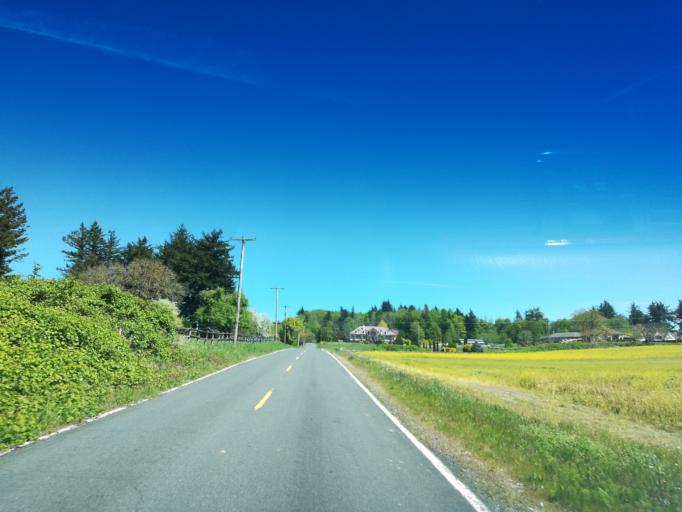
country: US
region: Oregon
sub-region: Multnomah County
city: Troutdale
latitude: 45.5335
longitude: -122.3545
